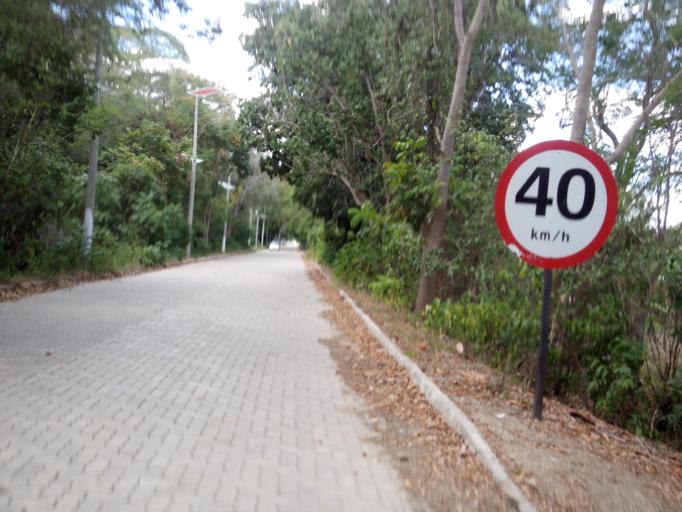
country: BR
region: Ceara
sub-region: Quixada
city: Quixada
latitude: -4.9790
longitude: -39.0611
